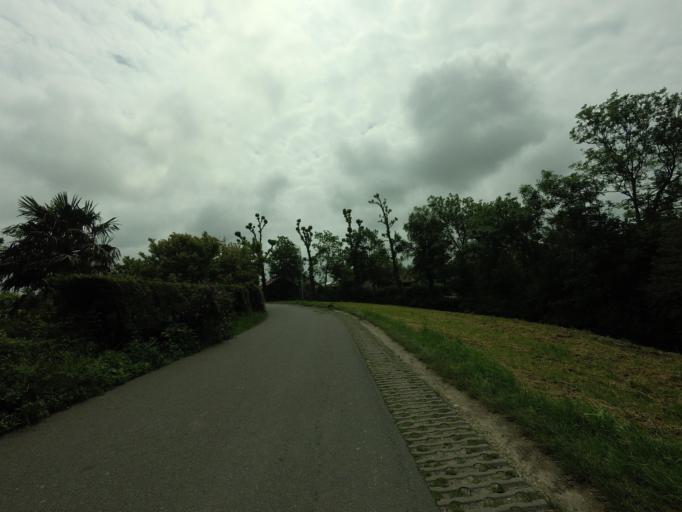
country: NL
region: North Holland
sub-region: Gemeente Schagen
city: Schagen
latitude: 52.7905
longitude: 4.7698
